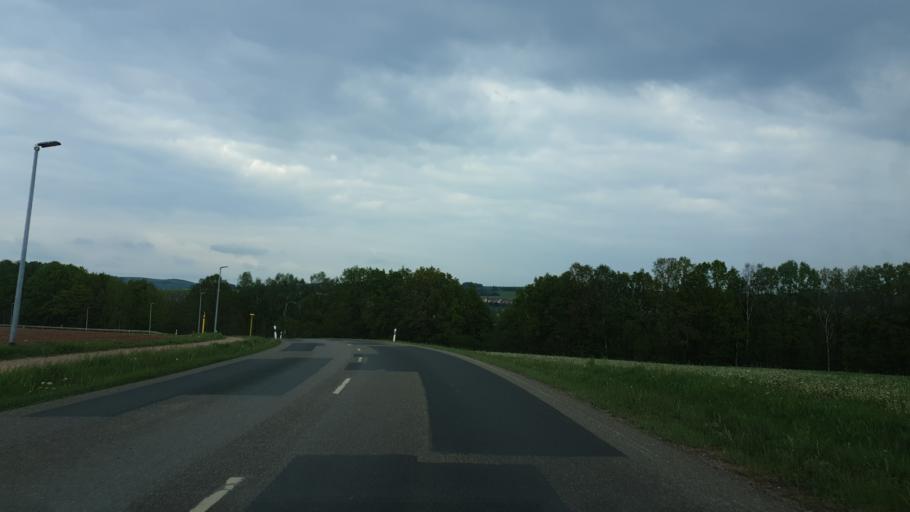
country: DE
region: Saxony
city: Neukirchen
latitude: 50.7671
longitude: 12.8639
